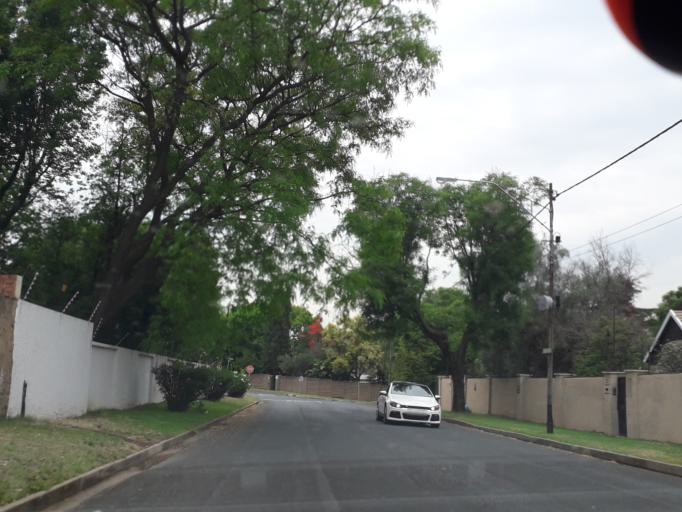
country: ZA
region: Gauteng
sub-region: City of Johannesburg Metropolitan Municipality
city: Johannesburg
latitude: -26.1290
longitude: 28.0783
